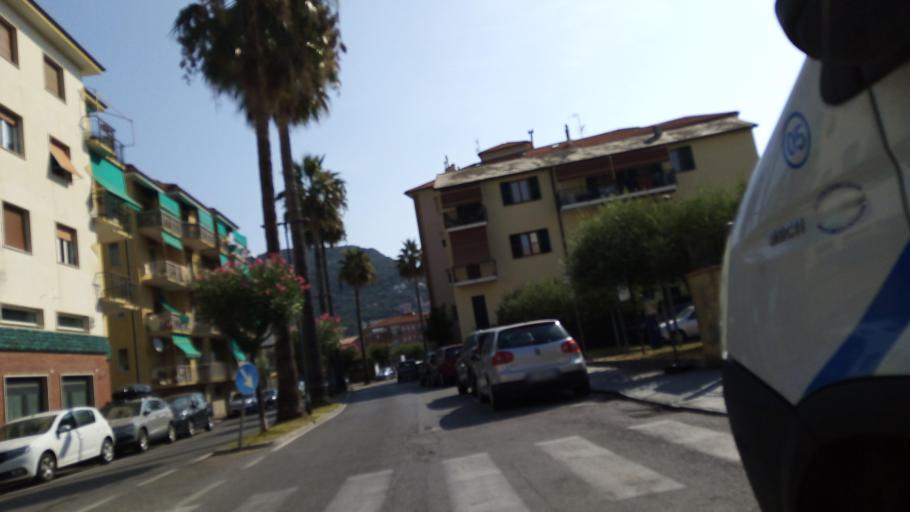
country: IT
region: Liguria
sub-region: Provincia di Savona
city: Borgio
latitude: 44.1580
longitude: 8.3043
